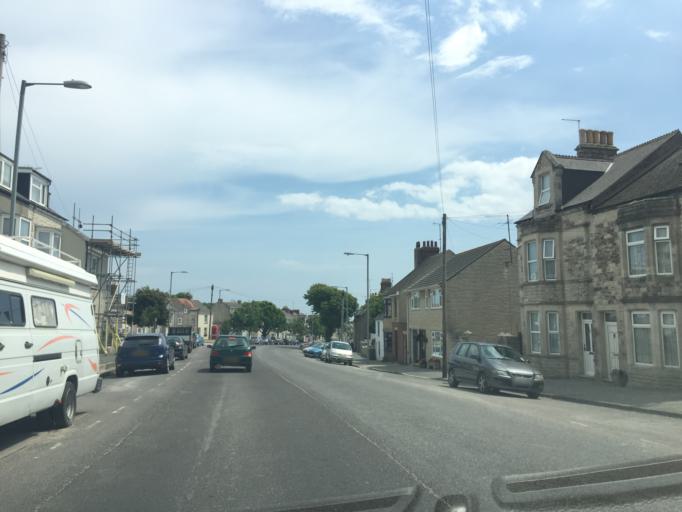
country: GB
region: England
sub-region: Dorset
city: Fortuneswell
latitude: 50.5433
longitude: -2.4320
